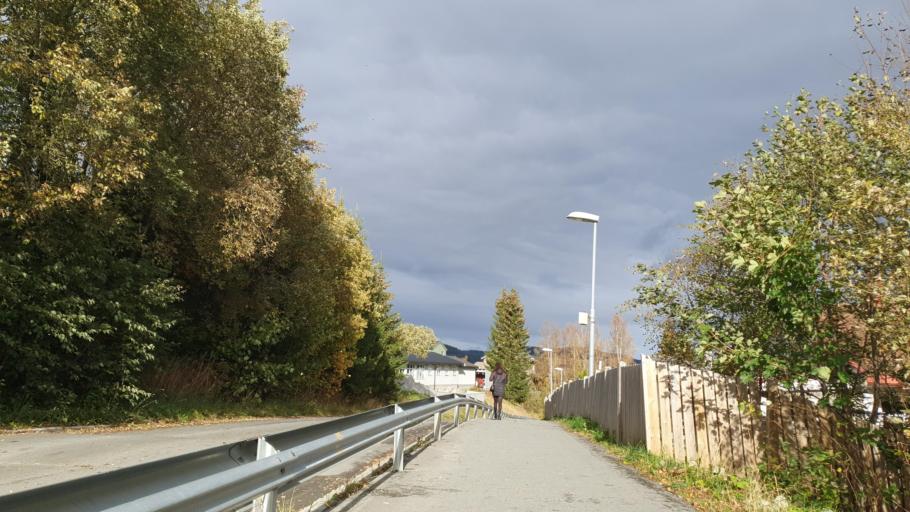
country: NO
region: Sor-Trondelag
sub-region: Klaebu
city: Klaebu
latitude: 63.3025
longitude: 10.4608
